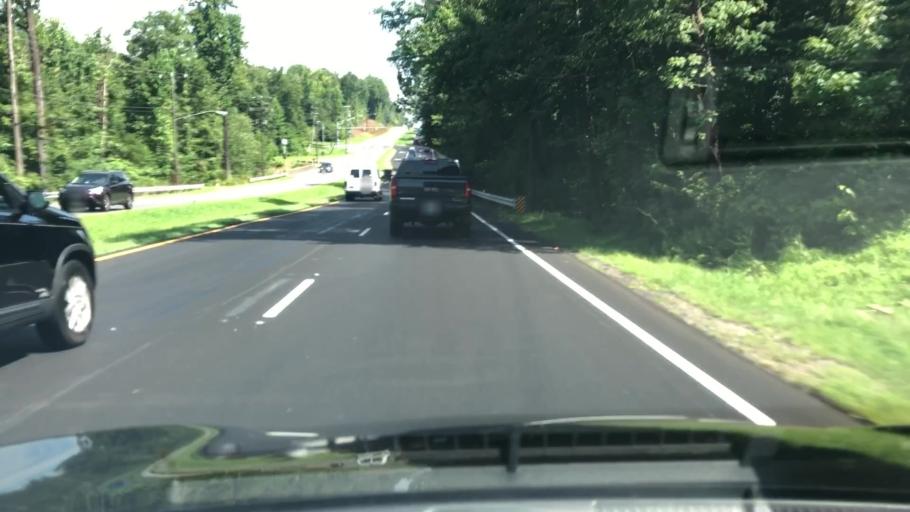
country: US
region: Virginia
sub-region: City of Fredericksburg
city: Fredericksburg
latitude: 38.2867
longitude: -77.4871
